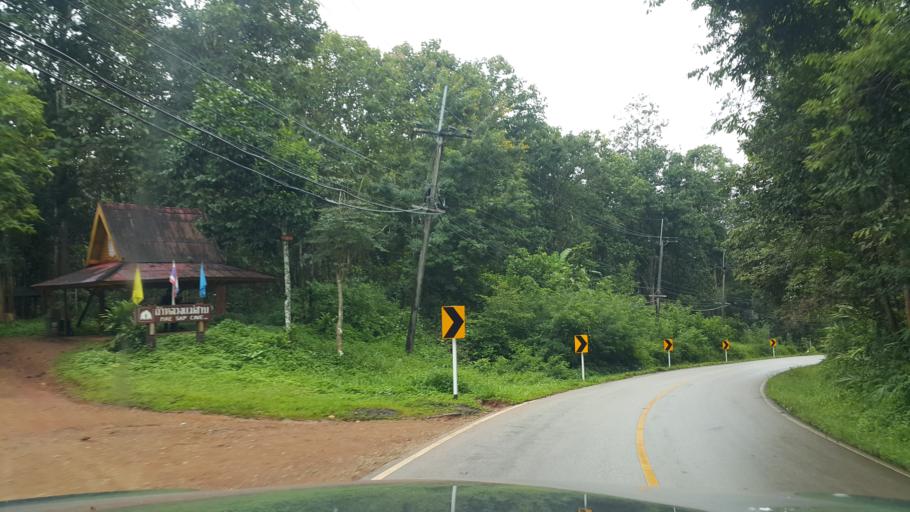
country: TH
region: Chiang Mai
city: Samoeng
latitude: 18.8631
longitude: 98.7129
